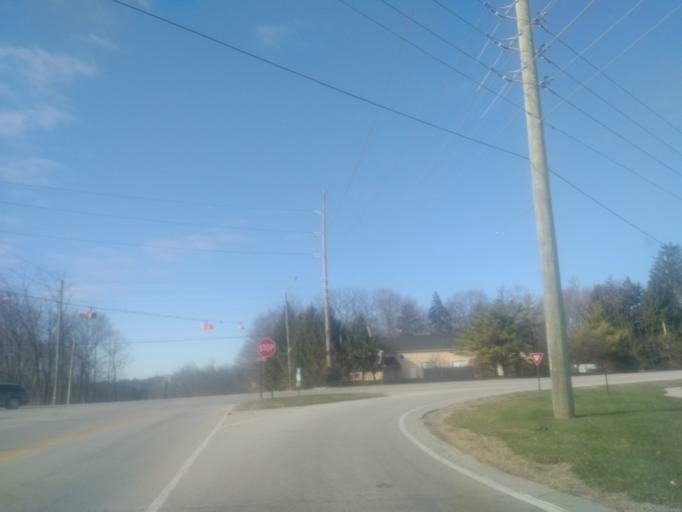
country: US
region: Indiana
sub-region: Boone County
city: Zionsville
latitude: 39.9098
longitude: -86.3110
